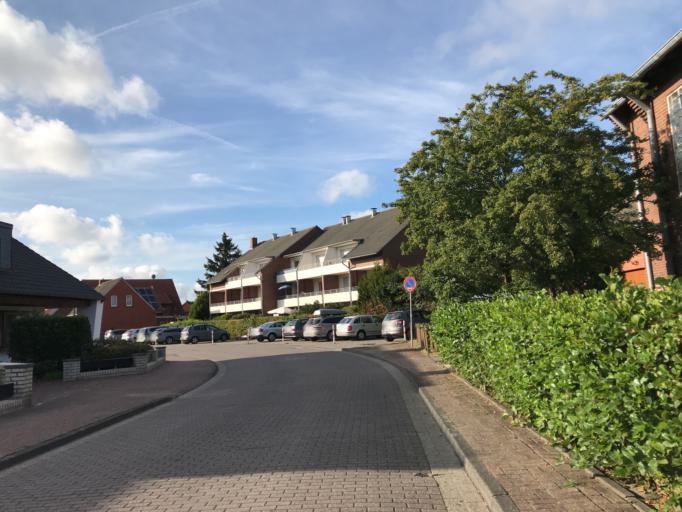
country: DE
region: Lower Saxony
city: Borkum
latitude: 53.5847
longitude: 6.6743
